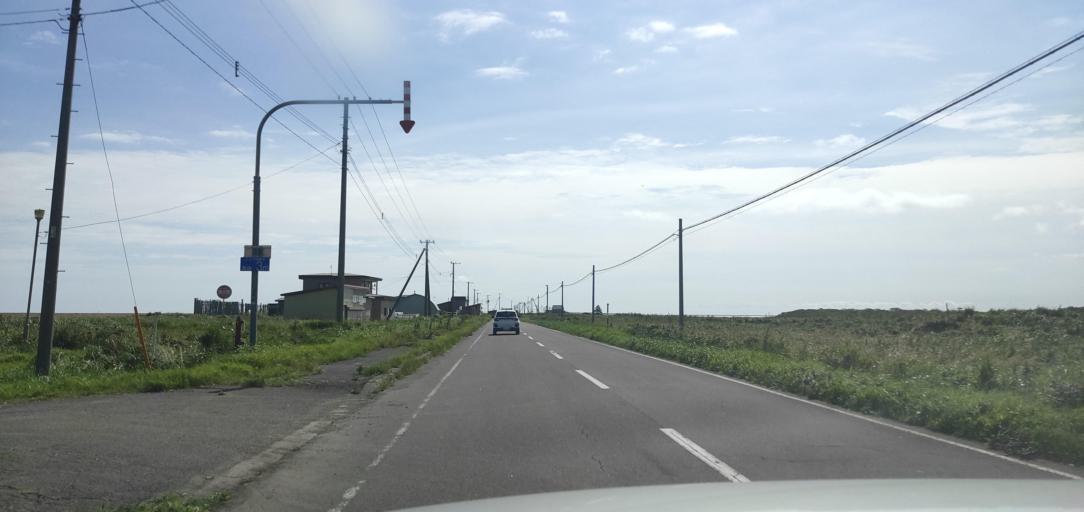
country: JP
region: Hokkaido
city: Shibetsu
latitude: 43.6319
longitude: 145.1856
